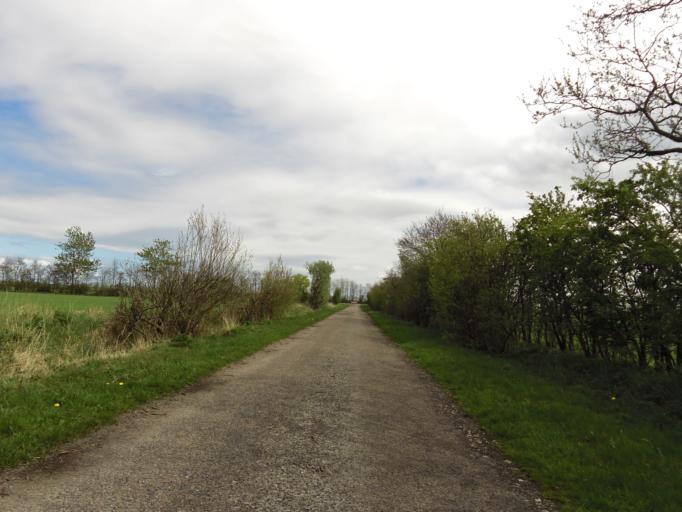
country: DK
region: South Denmark
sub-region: Haderslev Kommune
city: Gram
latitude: 55.2508
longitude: 9.0357
